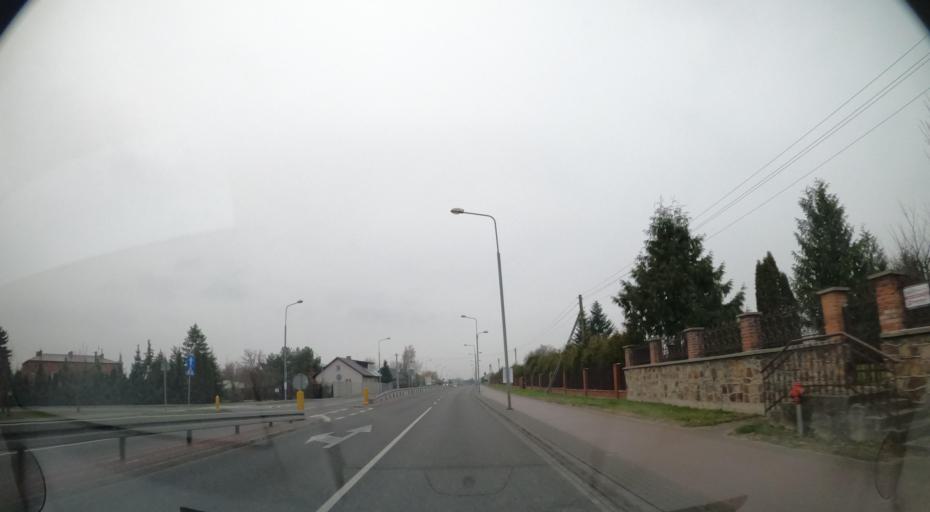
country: PL
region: Masovian Voivodeship
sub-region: Radom
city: Radom
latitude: 51.4229
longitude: 21.2166
